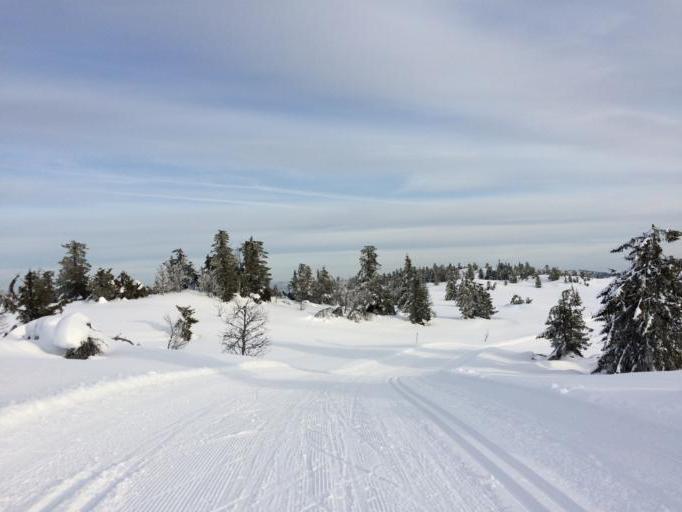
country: NO
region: Oppland
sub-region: Gausdal
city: Segalstad bru
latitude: 61.3269
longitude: 10.0372
